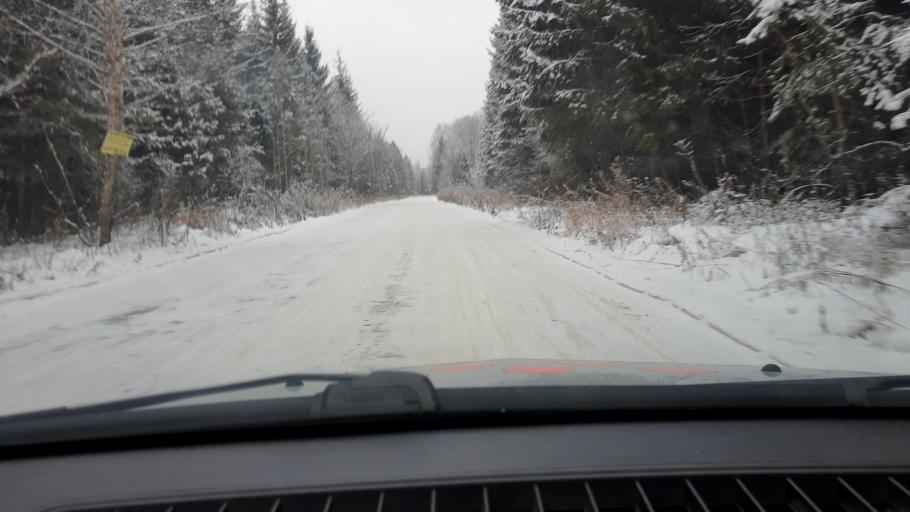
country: RU
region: Bashkortostan
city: Iglino
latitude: 54.8334
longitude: 56.2070
